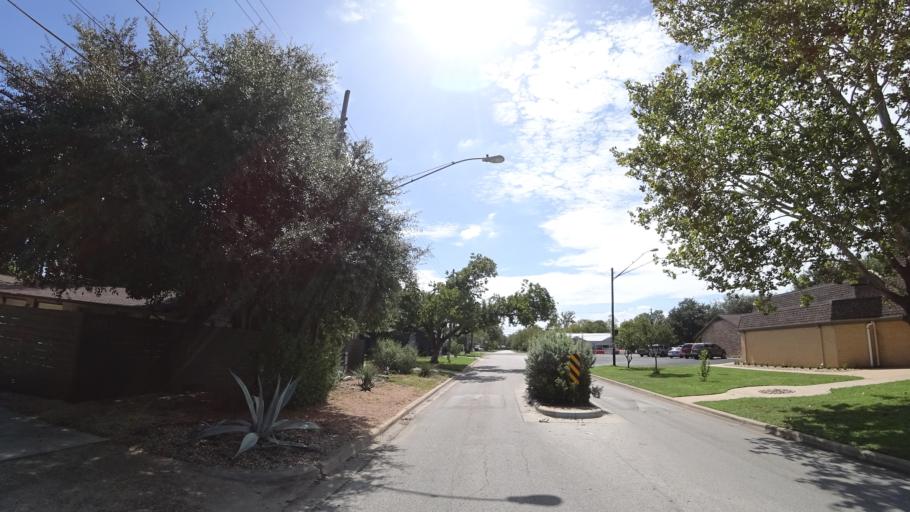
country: US
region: Texas
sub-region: Travis County
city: Austin
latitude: 30.3446
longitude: -97.7338
